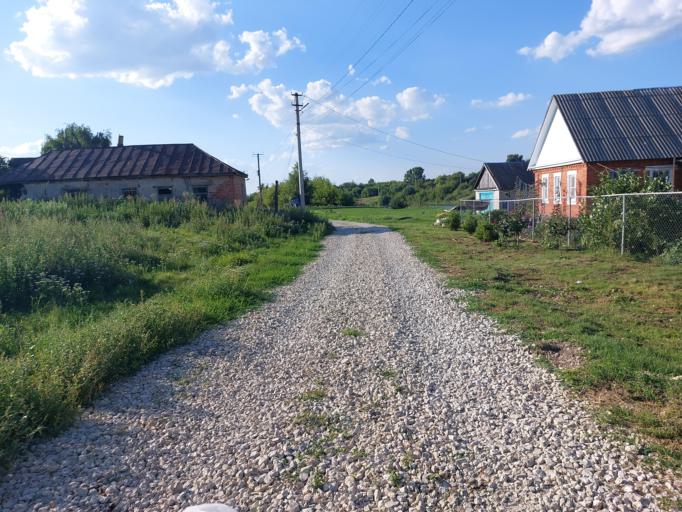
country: RU
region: Lipetsk
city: Terbuny
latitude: 52.2743
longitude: 38.1967
